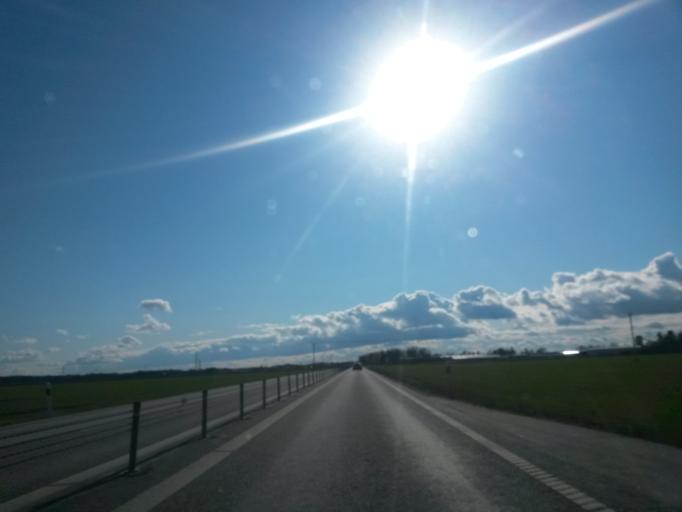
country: SE
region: Vaestra Goetaland
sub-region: Vara Kommun
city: Vara
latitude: 58.2643
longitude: 12.9913
